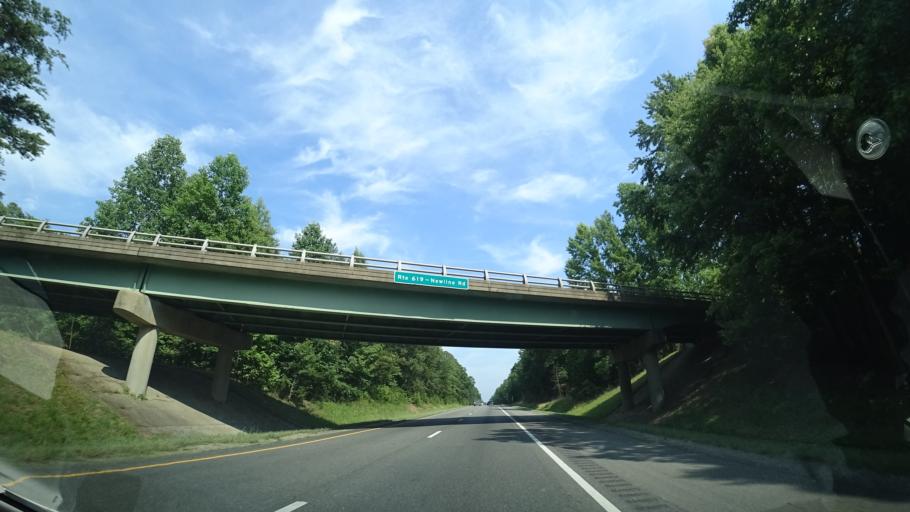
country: US
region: Virginia
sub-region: Goochland County
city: Goochland
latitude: 37.8054
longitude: -77.9263
